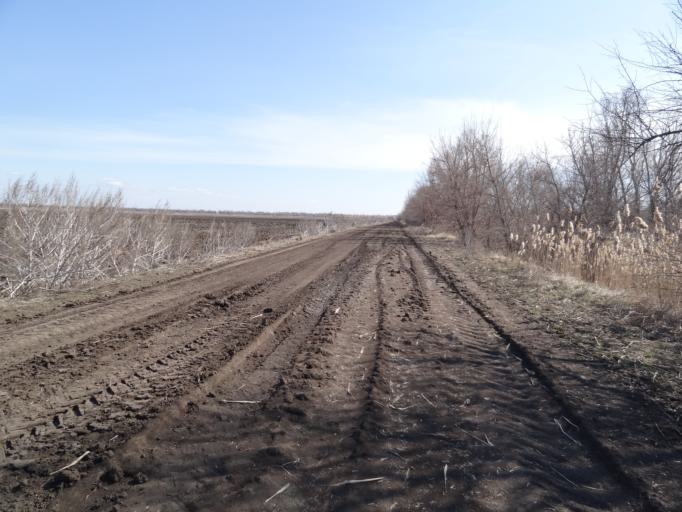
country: RU
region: Saratov
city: Engel's
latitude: 51.4182
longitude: 46.2143
